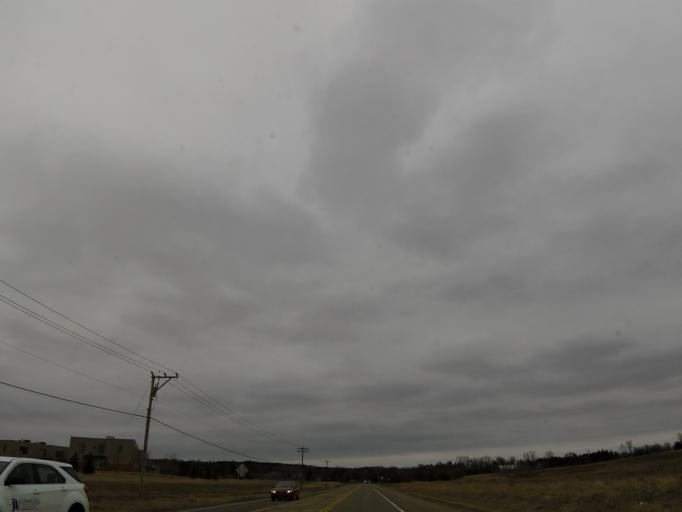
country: US
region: Minnesota
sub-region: Washington County
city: Bayport
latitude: 45.0120
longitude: -92.7959
